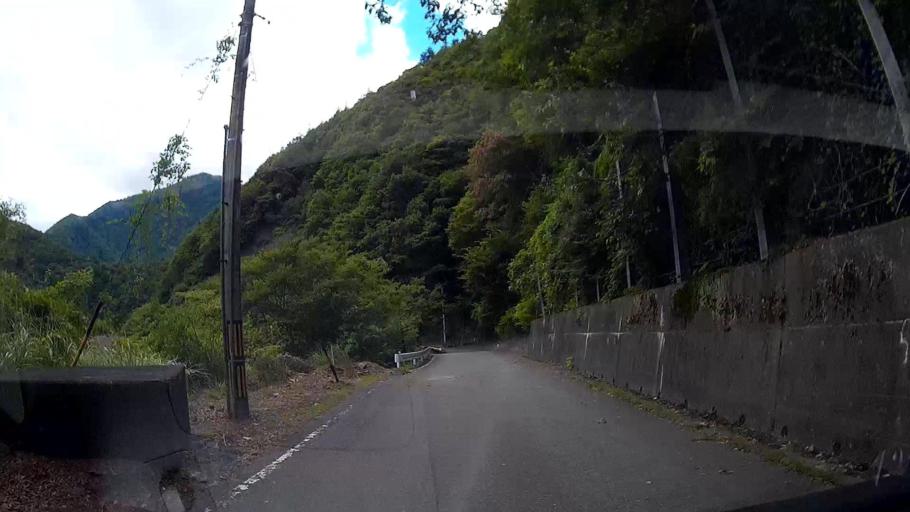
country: JP
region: Shizuoka
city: Shizuoka-shi
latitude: 35.3254
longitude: 138.1815
